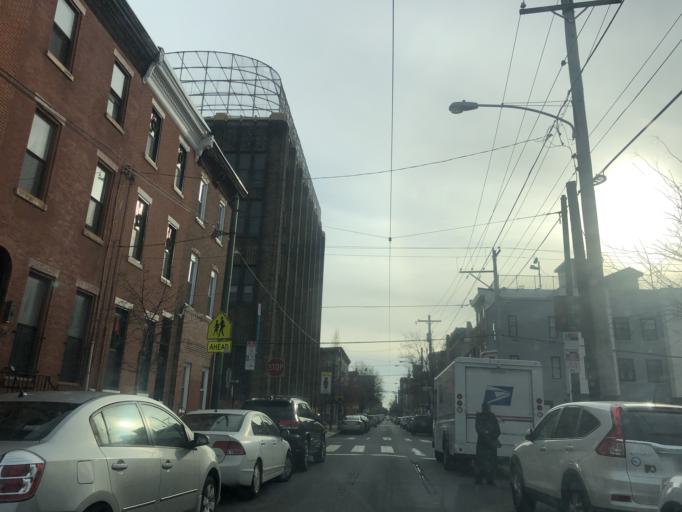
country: US
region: Pennsylvania
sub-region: Philadelphia County
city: Philadelphia
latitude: 39.9407
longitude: -75.1624
